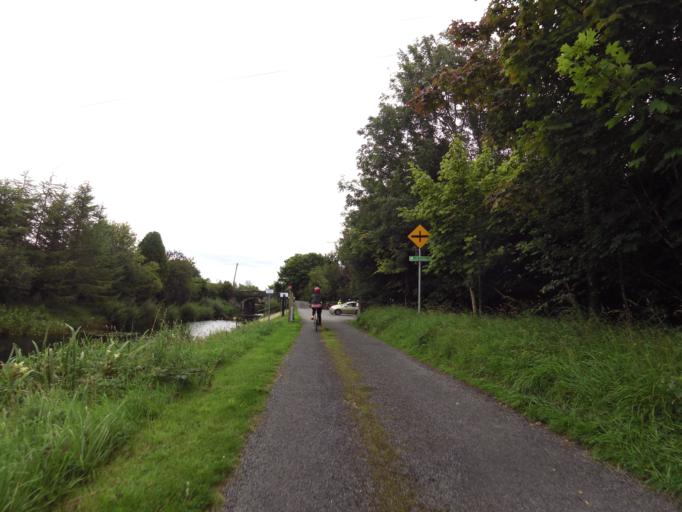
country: IE
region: Leinster
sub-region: An Iarmhi
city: An Muileann gCearr
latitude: 53.5350
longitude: -7.4694
